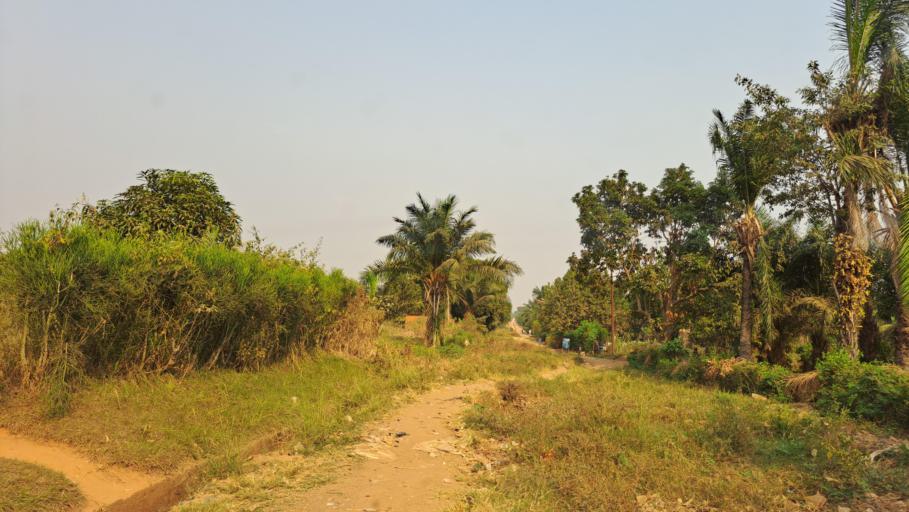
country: CD
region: Kasai-Oriental
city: Mbuji-Mayi
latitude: -6.1353
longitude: 23.5885
